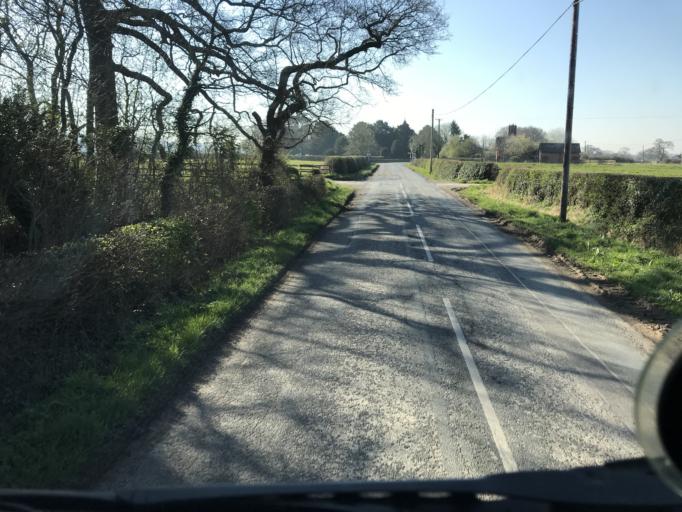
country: GB
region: England
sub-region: Cheshire West and Chester
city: Aldford
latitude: 53.1411
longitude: -2.8422
